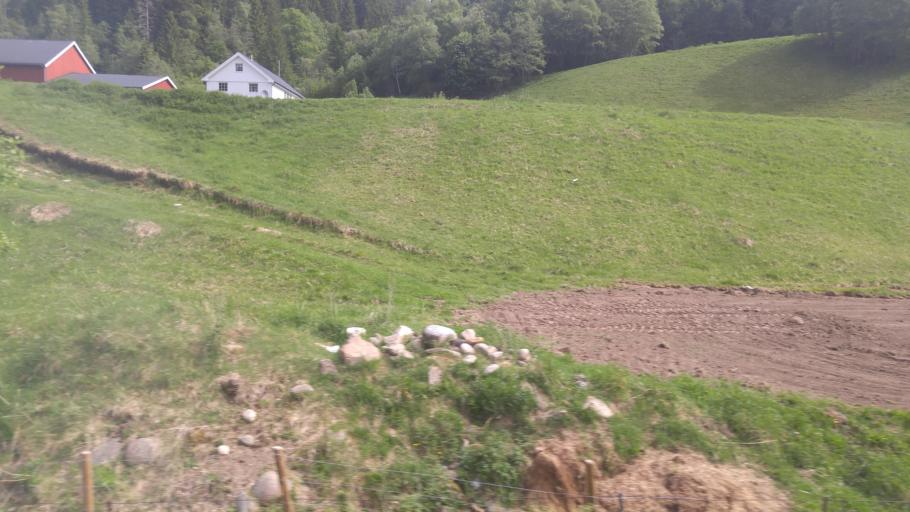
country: NO
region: Sor-Trondelag
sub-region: Midtre Gauldal
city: Storen
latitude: 63.0017
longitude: 10.4630
